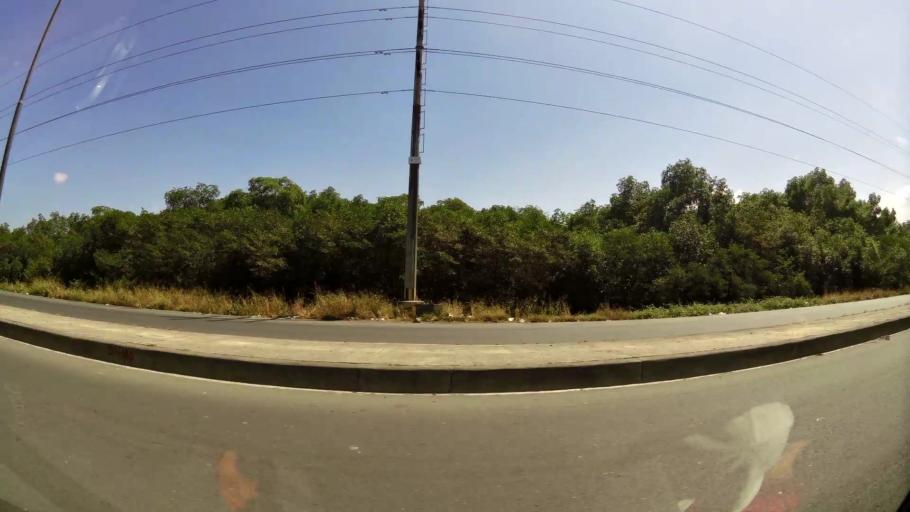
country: EC
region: Guayas
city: Guayaquil
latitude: -2.2174
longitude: -79.9567
